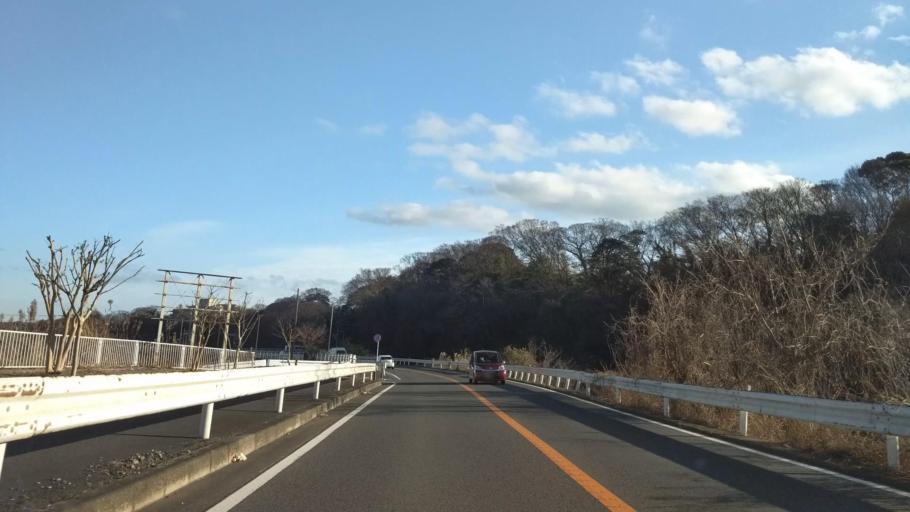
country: JP
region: Kanagawa
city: Hadano
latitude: 35.3590
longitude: 139.2516
